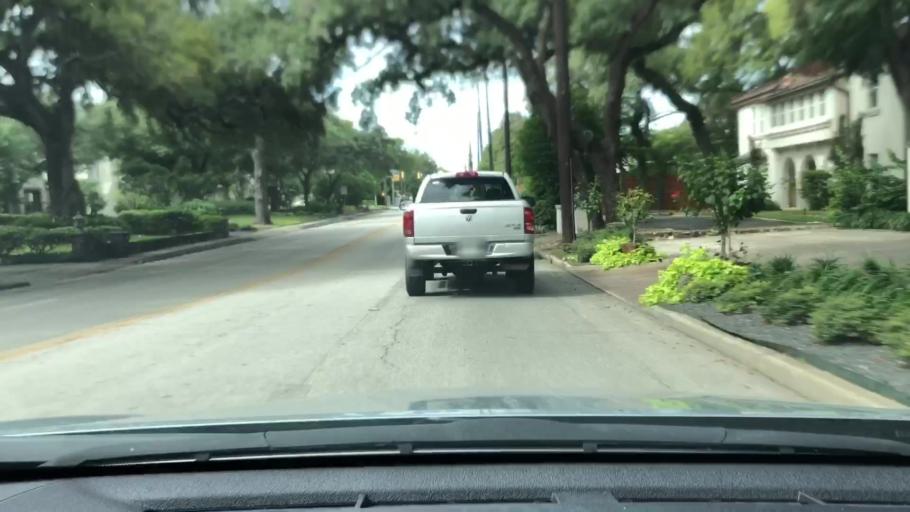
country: US
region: Texas
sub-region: Bexar County
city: Olmos Park
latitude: 29.4666
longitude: -98.4856
